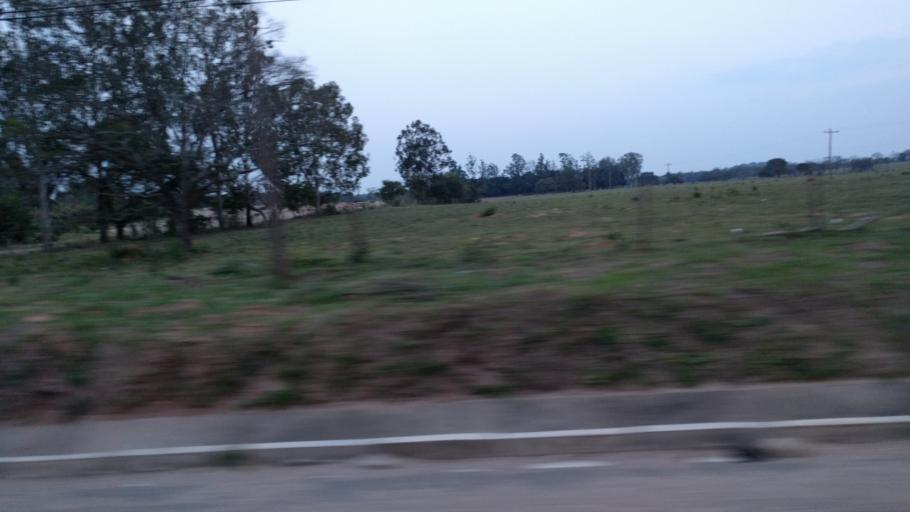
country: BO
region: Santa Cruz
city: Santa Rita
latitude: -17.8895
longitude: -63.3077
